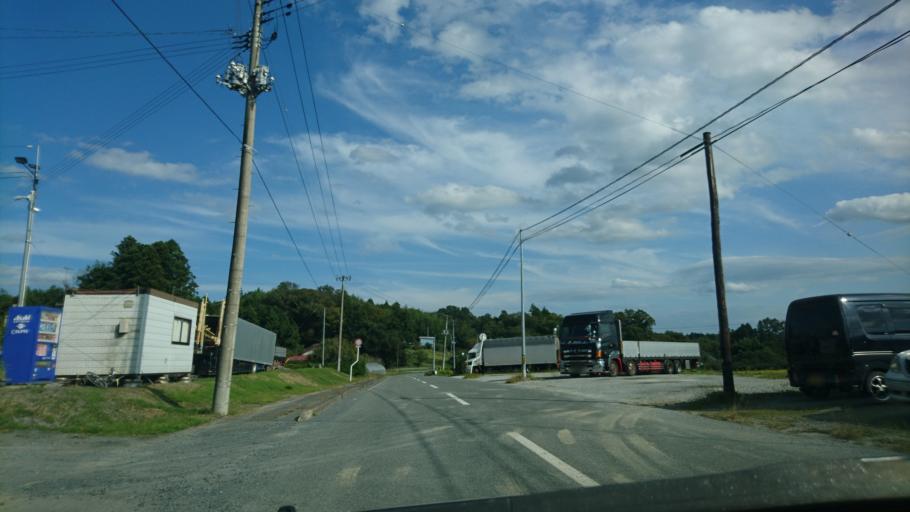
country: JP
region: Iwate
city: Ichinoseki
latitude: 38.8431
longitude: 141.1857
